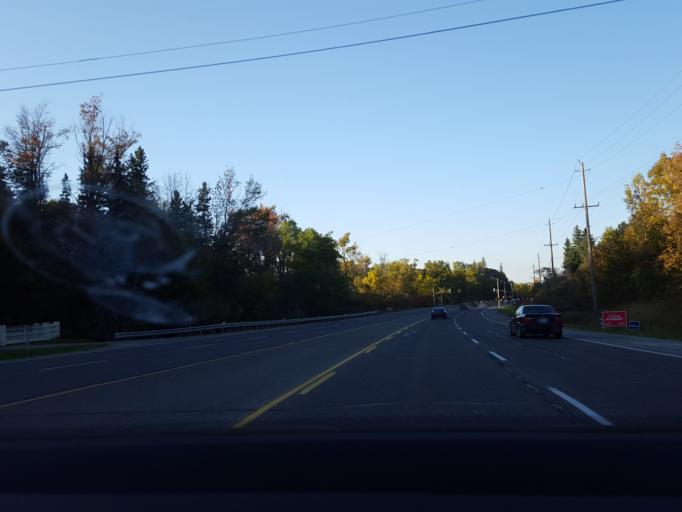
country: CA
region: Ontario
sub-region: York
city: Richmond Hill
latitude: 43.9328
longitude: -79.4529
